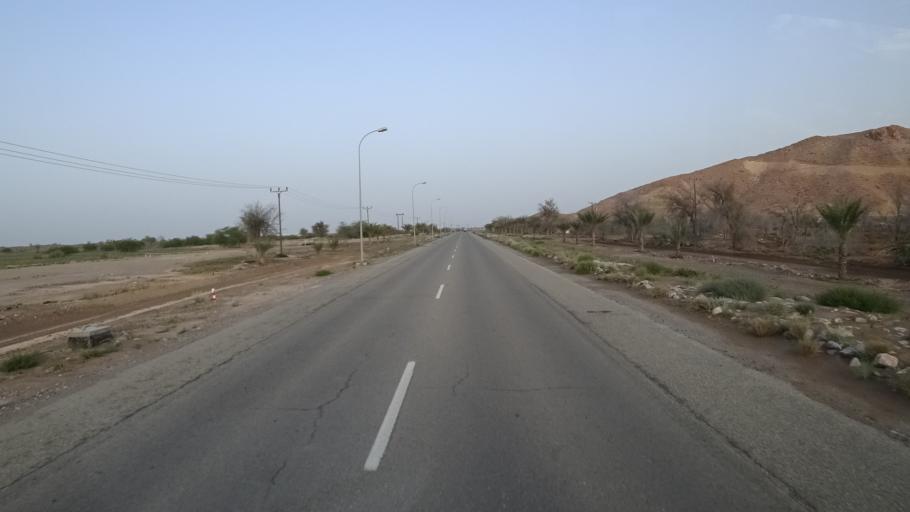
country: OM
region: Muhafazat Masqat
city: Muscat
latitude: 23.2163
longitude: 58.9288
